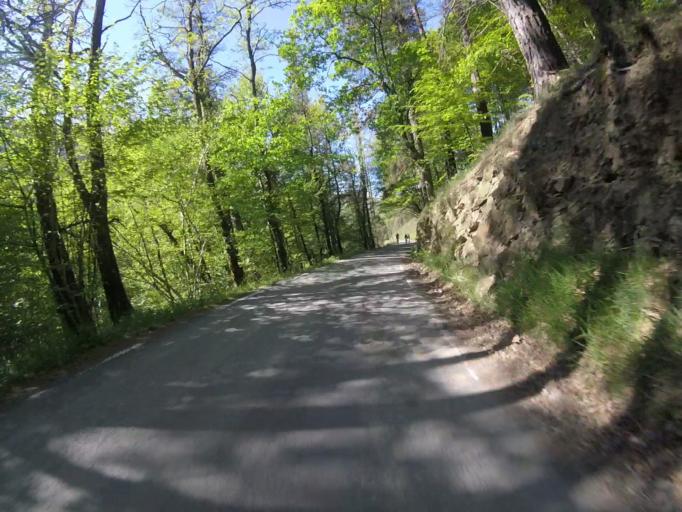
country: ES
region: Basque Country
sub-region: Provincia de Guipuzcoa
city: Errezil
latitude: 43.1876
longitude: -2.1969
